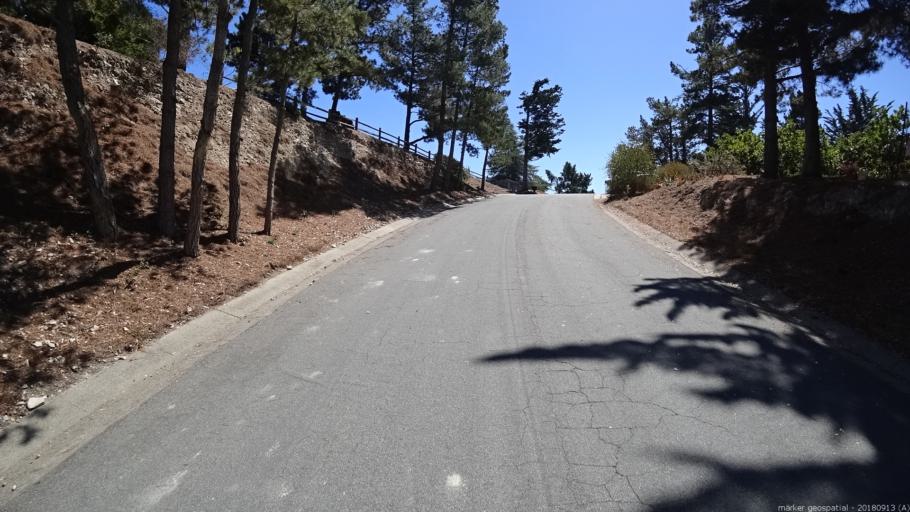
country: US
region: California
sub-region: Monterey County
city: Carmel Valley Village
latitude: 36.5410
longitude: -121.7968
